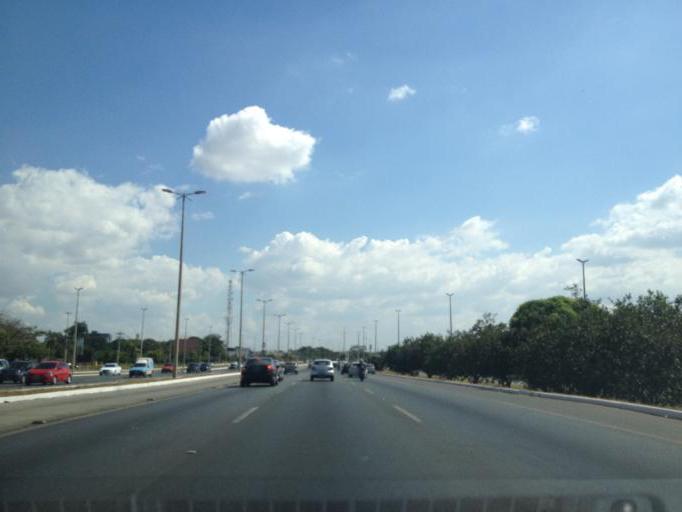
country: BR
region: Federal District
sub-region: Brasilia
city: Brasilia
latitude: -15.8119
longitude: -47.9797
